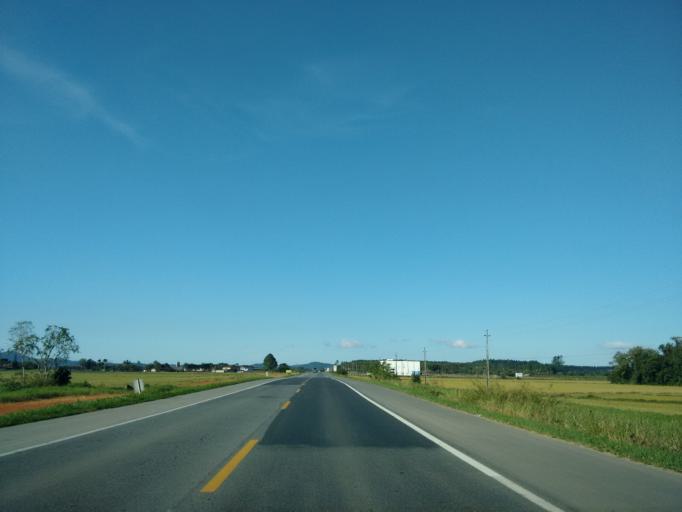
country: BR
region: Santa Catarina
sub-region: Guaramirim
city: Guaramirim
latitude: -26.4516
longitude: -48.8834
